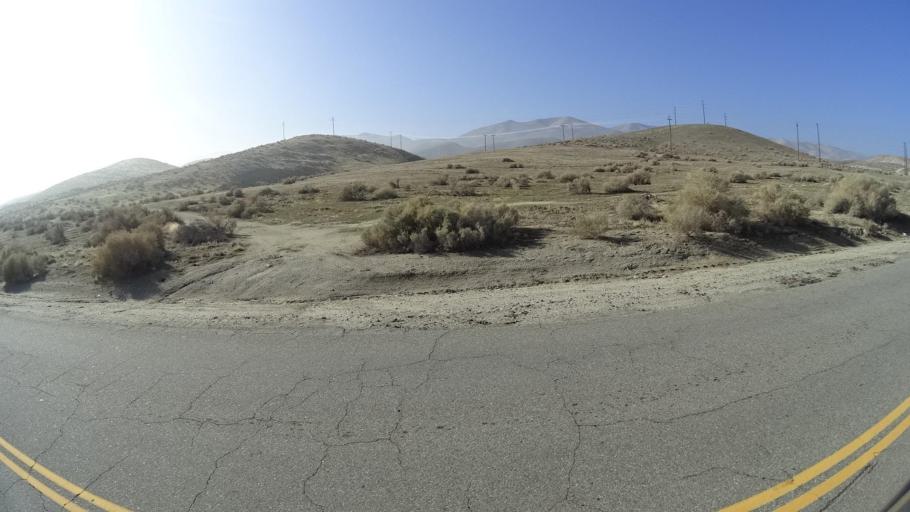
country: US
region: California
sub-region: Kern County
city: Taft Heights
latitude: 35.1926
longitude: -119.5788
